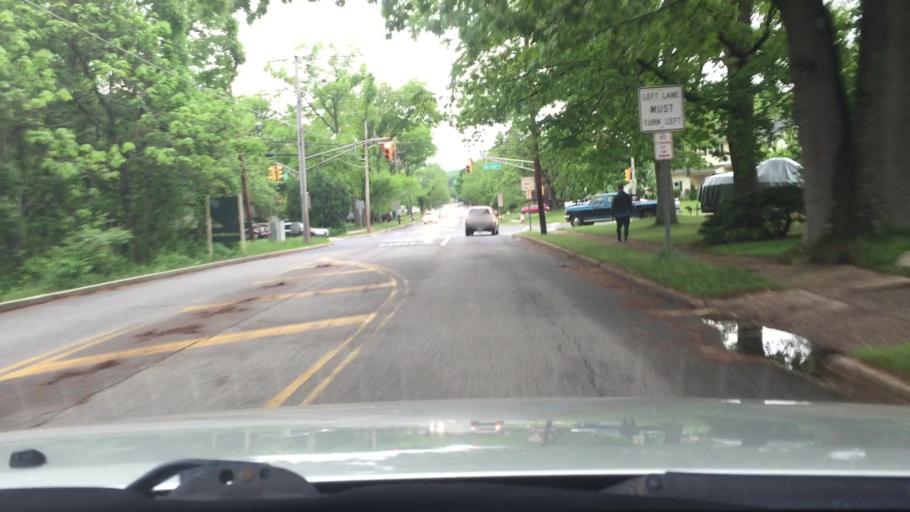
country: US
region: New Jersey
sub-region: Middlesex County
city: Spotswood
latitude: 40.4019
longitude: -74.4025
